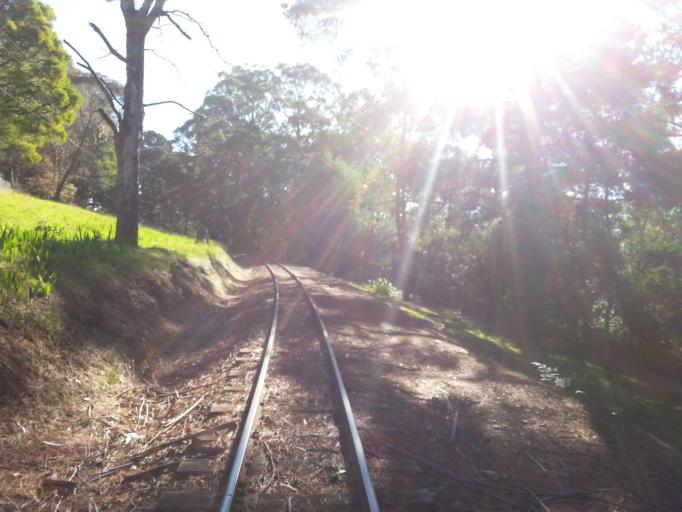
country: AU
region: Victoria
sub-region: Cardinia
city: Emerald
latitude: -37.9328
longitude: 145.4519
